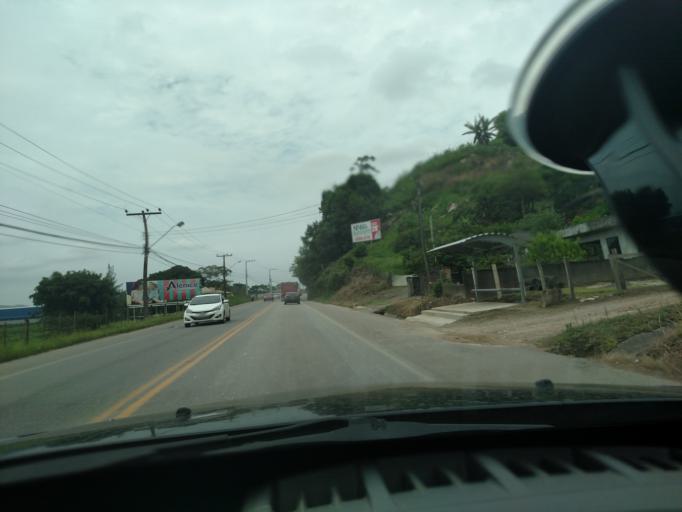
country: BR
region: Santa Catarina
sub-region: Itajai
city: Itajai
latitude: -26.8861
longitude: -48.7432
